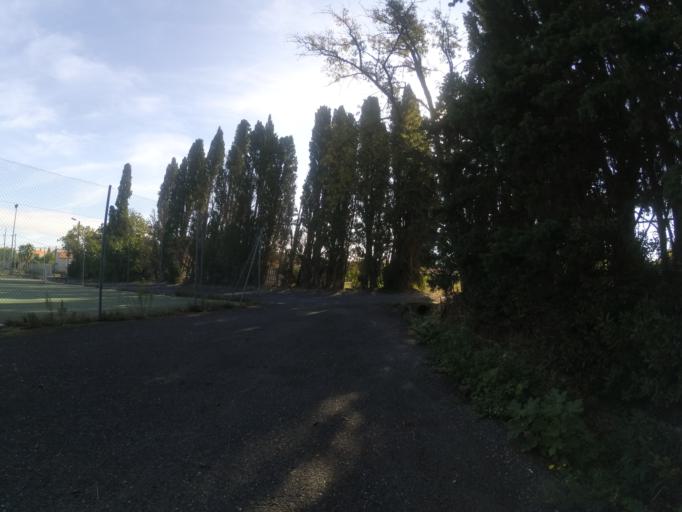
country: FR
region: Languedoc-Roussillon
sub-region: Departement des Pyrenees-Orientales
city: Pezilla-la-Riviere
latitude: 42.6926
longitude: 2.7628
